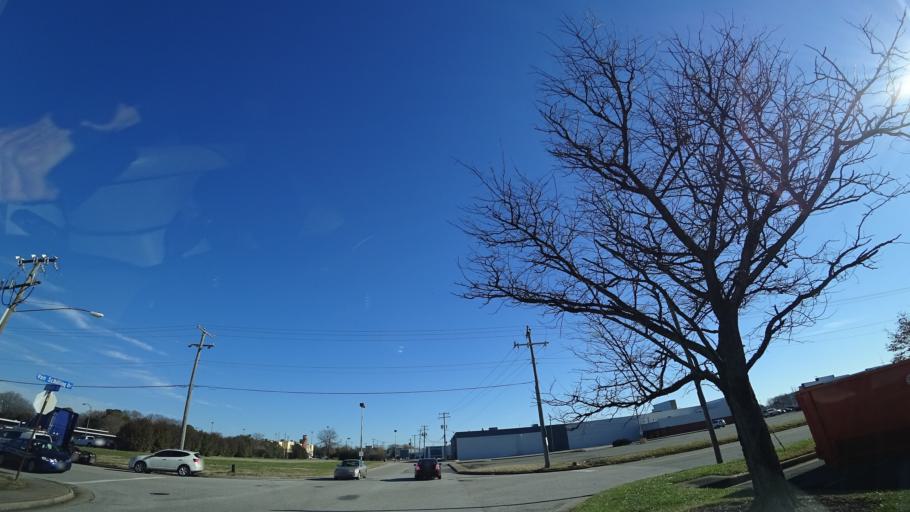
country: US
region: Virginia
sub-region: City of Hampton
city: Hampton
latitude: 37.0443
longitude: -76.3888
